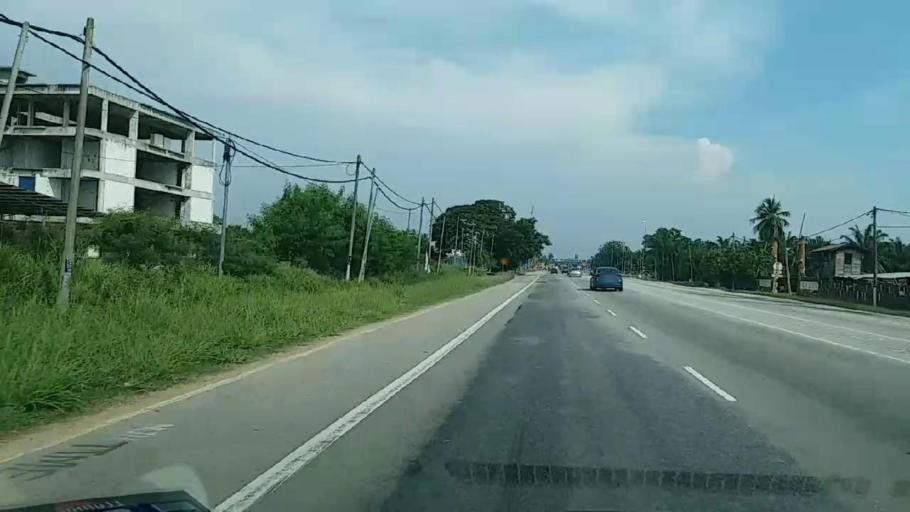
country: MY
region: Selangor
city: Kuala Selangor
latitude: 3.3669
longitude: 101.2442
